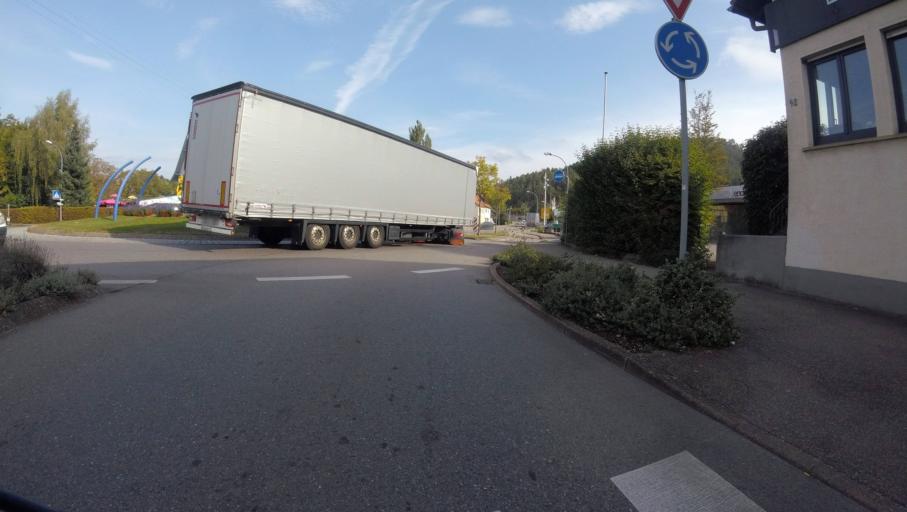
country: DE
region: Baden-Wuerttemberg
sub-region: Karlsruhe Region
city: Nagold
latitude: 48.5330
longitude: 8.7235
